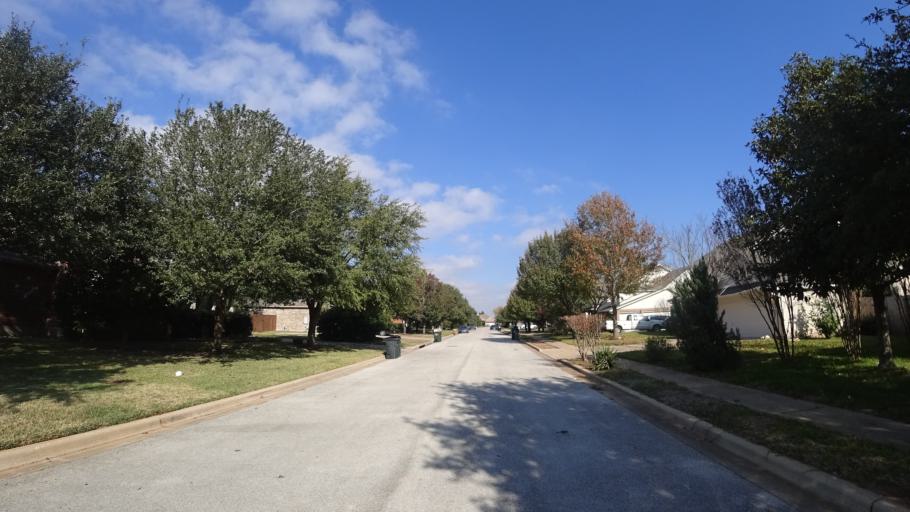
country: US
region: Texas
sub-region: Travis County
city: Shady Hollow
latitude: 30.1708
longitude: -97.8712
